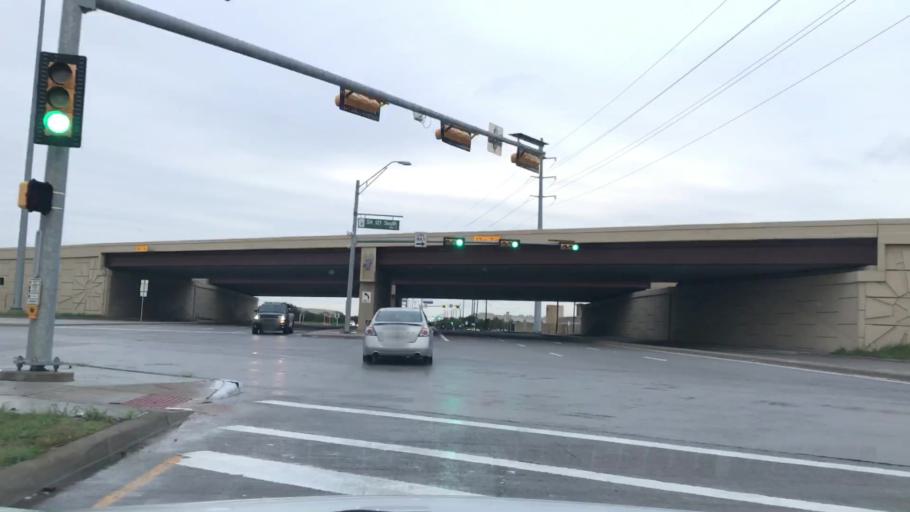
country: US
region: Texas
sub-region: Dallas County
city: Coppell
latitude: 32.9731
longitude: -97.0297
